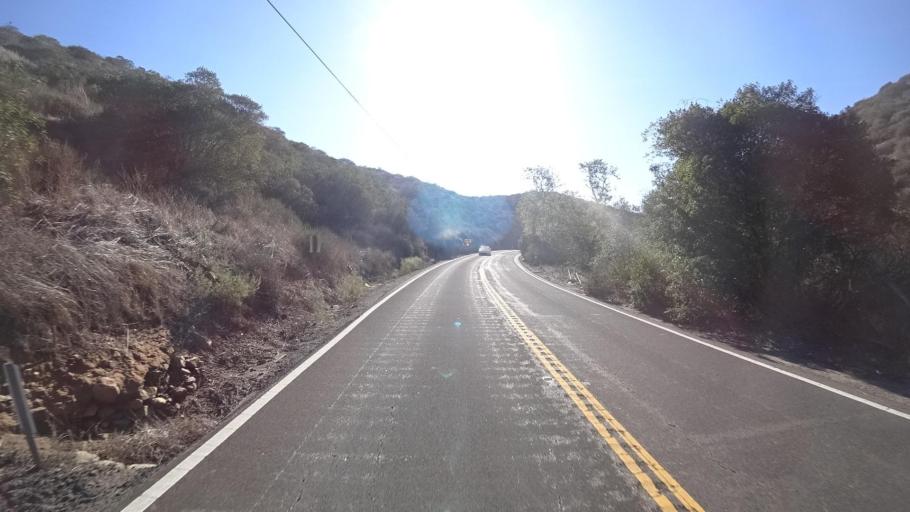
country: MX
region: Baja California
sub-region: Tijuana
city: El Nino
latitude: 32.6380
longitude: -116.7663
